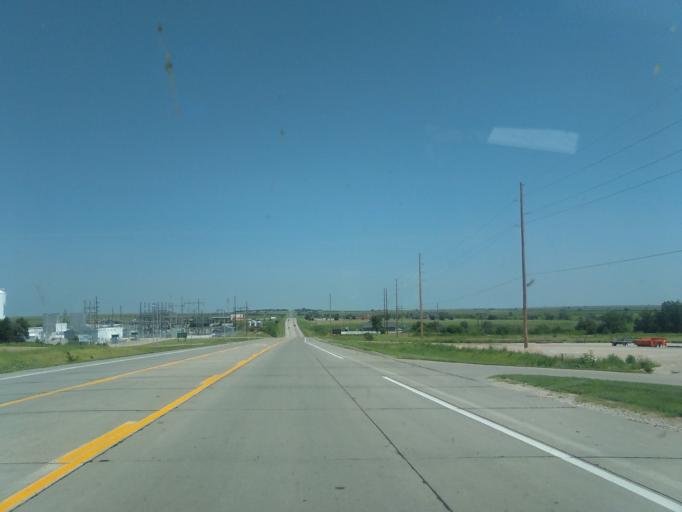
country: US
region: Nebraska
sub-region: Red Willow County
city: McCook
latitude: 40.2186
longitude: -100.6501
